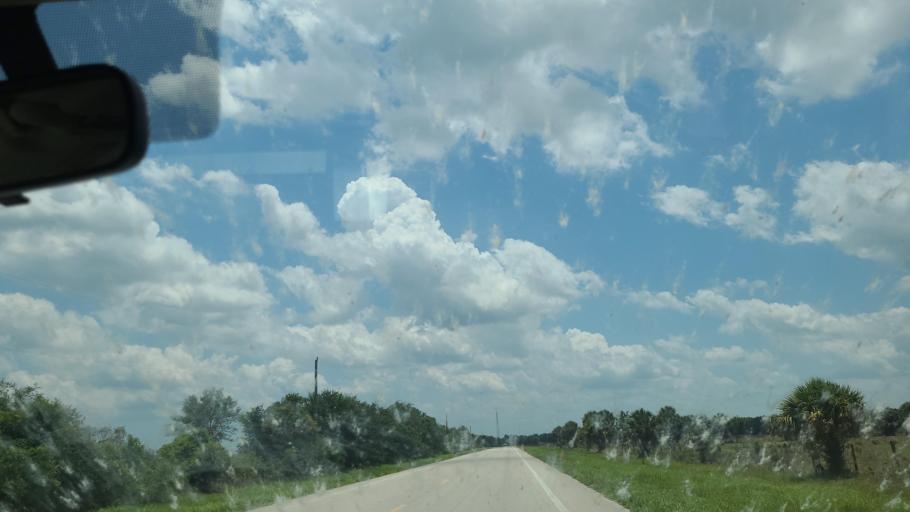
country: US
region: Florida
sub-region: Glades County
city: Buckhead Ridge
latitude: 27.1348
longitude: -81.0897
